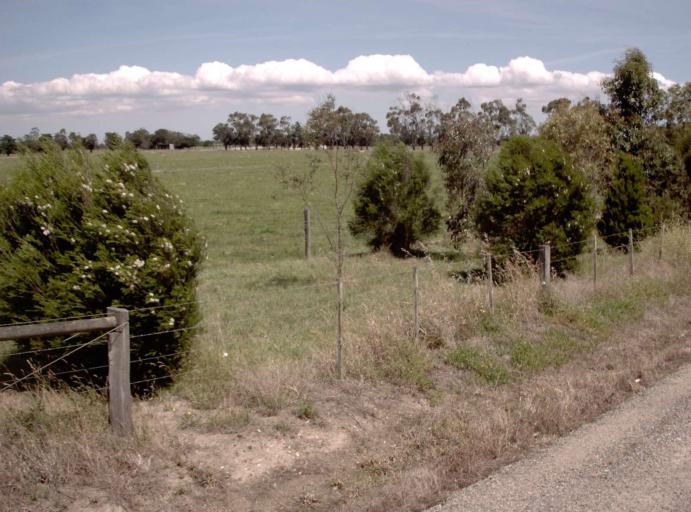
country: AU
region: Victoria
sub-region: Wellington
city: Heyfield
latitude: -38.0397
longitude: 146.8773
